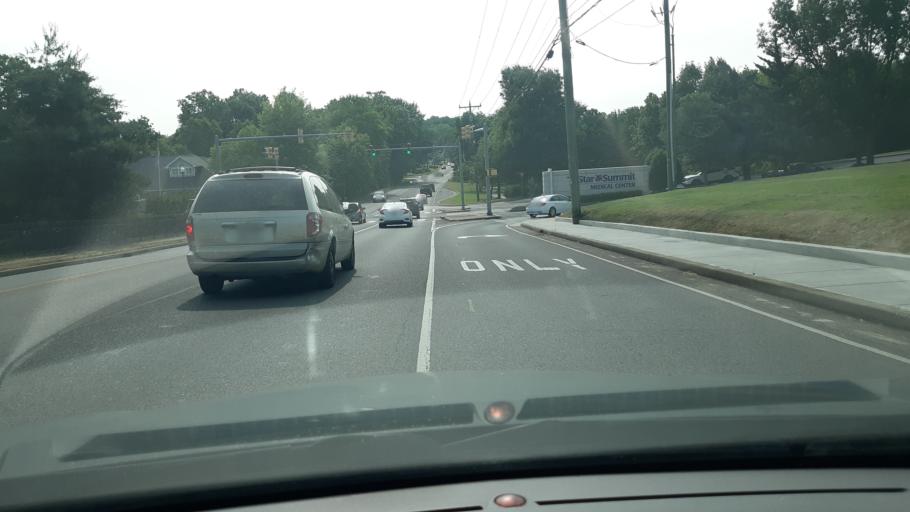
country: US
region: Tennessee
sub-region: Davidson County
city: Lakewood
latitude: 36.1742
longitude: -86.6079
